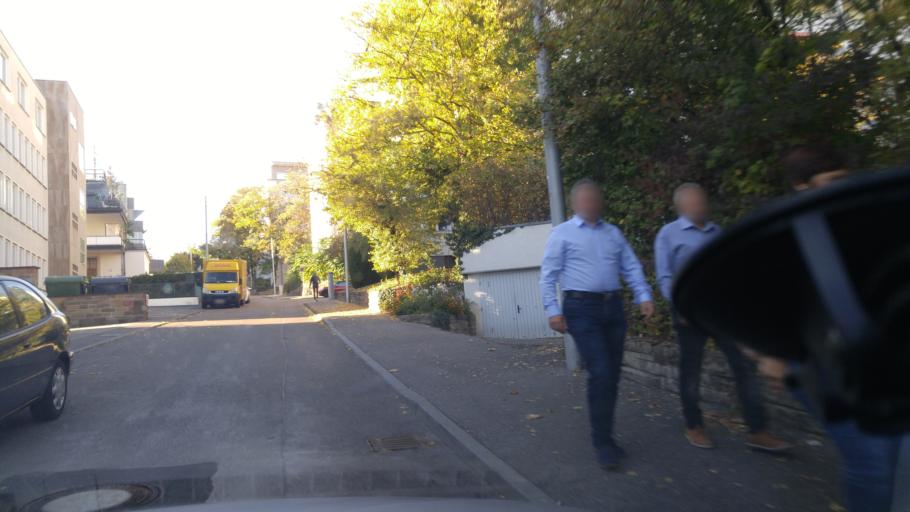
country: DE
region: Baden-Wuerttemberg
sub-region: Regierungsbezirk Stuttgart
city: Stuttgart
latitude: 48.7846
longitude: 9.1692
